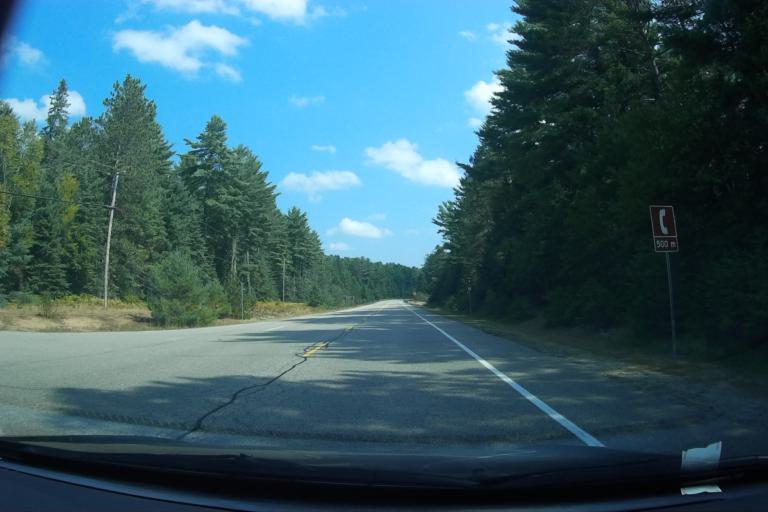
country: CA
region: Ontario
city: Huntsville
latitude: 45.5793
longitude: -78.5136
